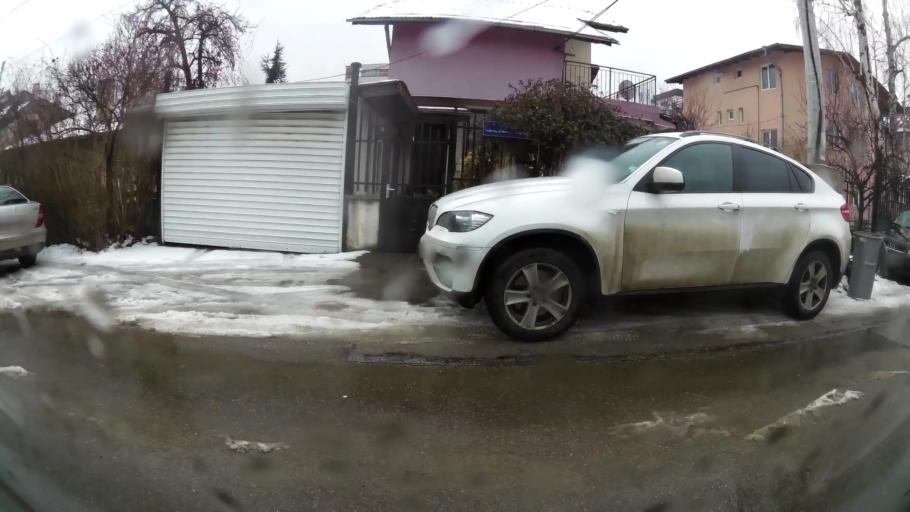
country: BG
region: Sofia-Capital
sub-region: Stolichna Obshtina
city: Sofia
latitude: 42.6606
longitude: 23.2752
